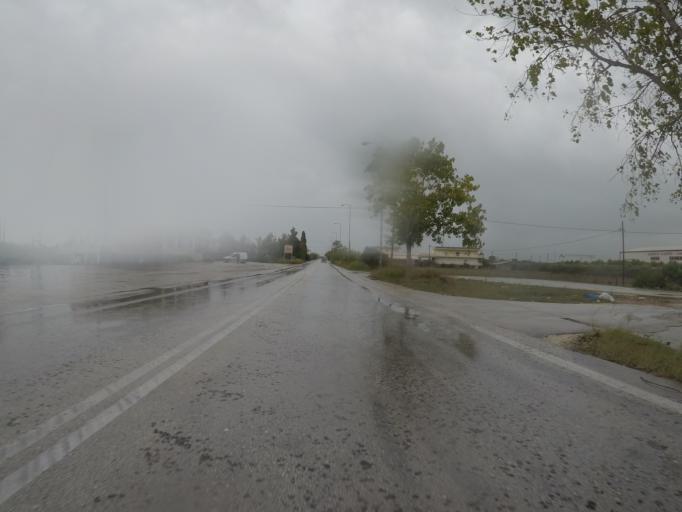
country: GR
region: Peloponnese
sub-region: Nomos Korinthias
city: Arkhaia Korinthos
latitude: 37.9183
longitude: 22.8843
